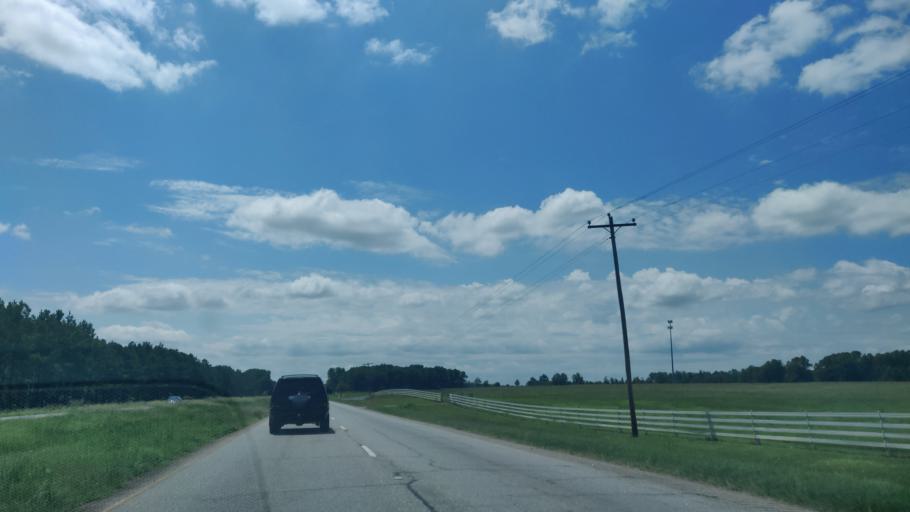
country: US
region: Georgia
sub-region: Stewart County
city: Richland
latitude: 32.0182
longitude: -84.6625
